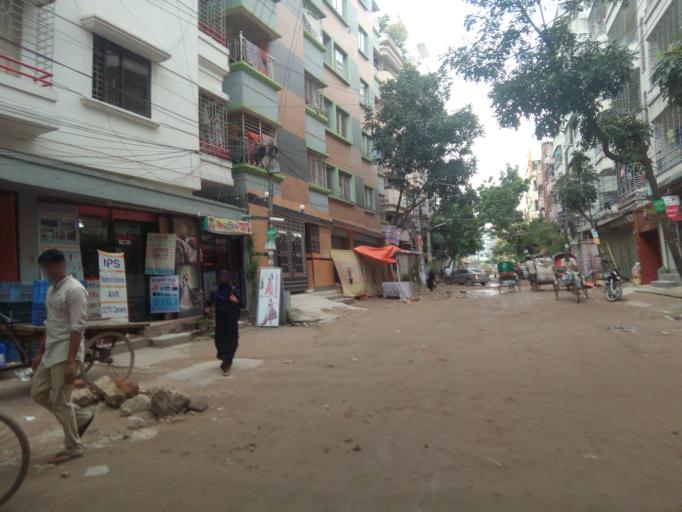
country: BD
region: Dhaka
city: Paltan
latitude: 23.8073
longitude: 90.4356
